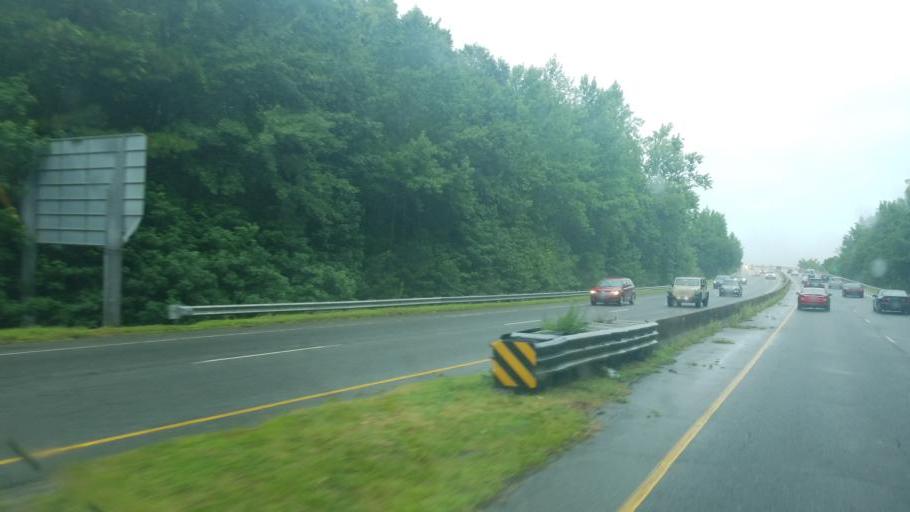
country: US
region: Virginia
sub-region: City of Chesapeake
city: Chesapeake
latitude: 36.7148
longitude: -76.2253
